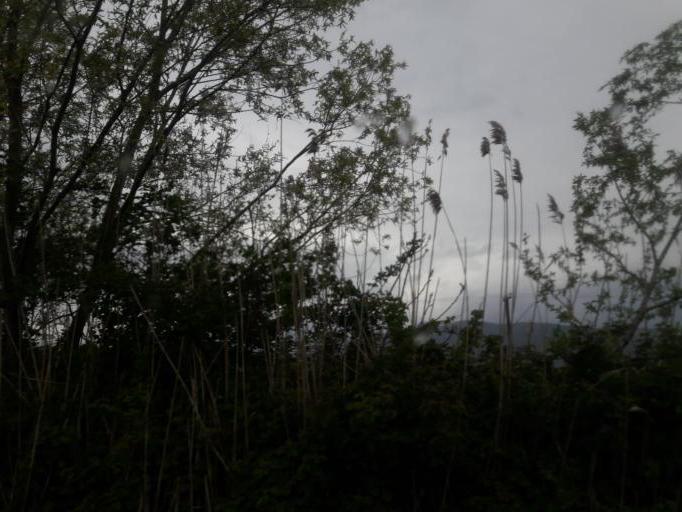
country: AL
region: Shkoder
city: Vukatane
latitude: 42.0060
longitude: 19.5360
